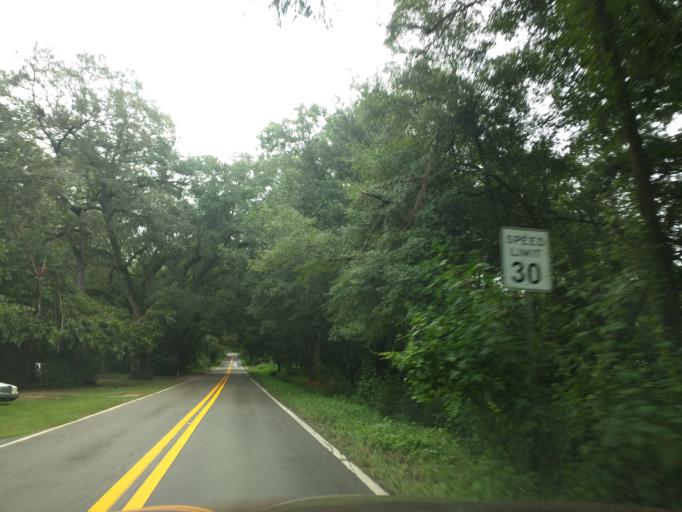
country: US
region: Florida
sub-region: Leon County
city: Tallahassee
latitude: 30.5216
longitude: -84.1192
